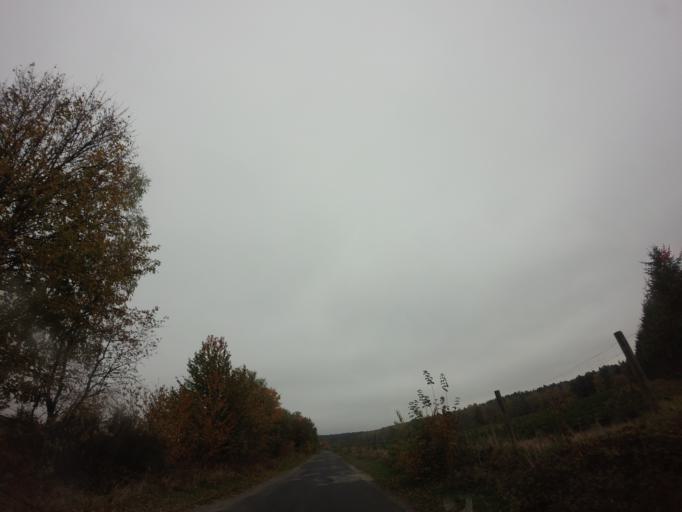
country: PL
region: West Pomeranian Voivodeship
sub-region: Powiat choszczenski
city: Bierzwnik
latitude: 53.1115
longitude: 15.6383
